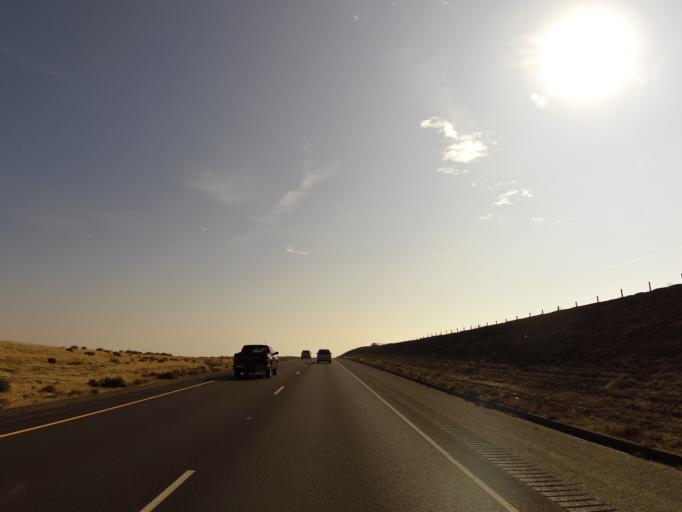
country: US
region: California
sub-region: Kings County
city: Kettleman City
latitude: 36.0227
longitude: -120.0110
